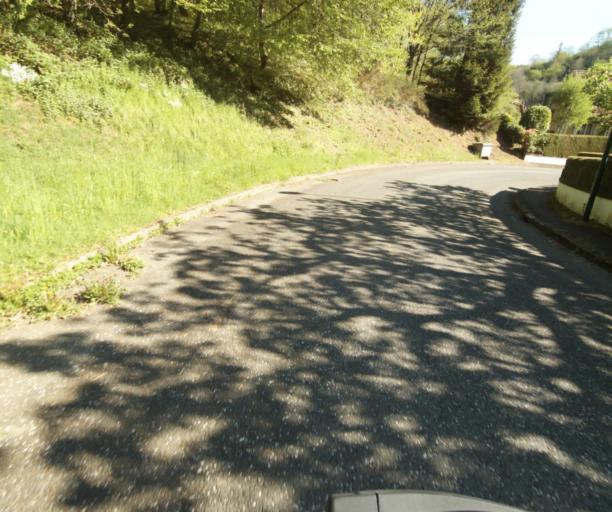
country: FR
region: Limousin
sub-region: Departement de la Correze
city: Tulle
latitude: 45.2831
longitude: 1.7854
